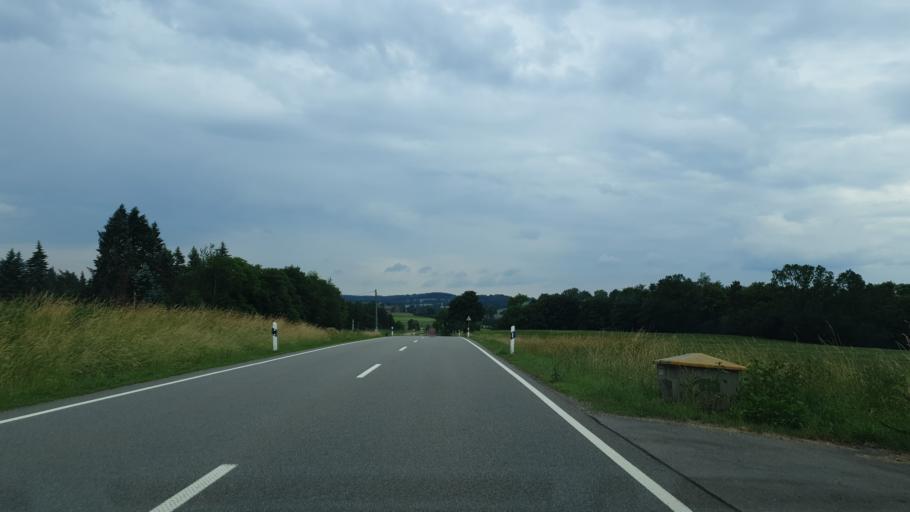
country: DE
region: Saxony
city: Hirschfeld
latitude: 50.6209
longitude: 12.4318
